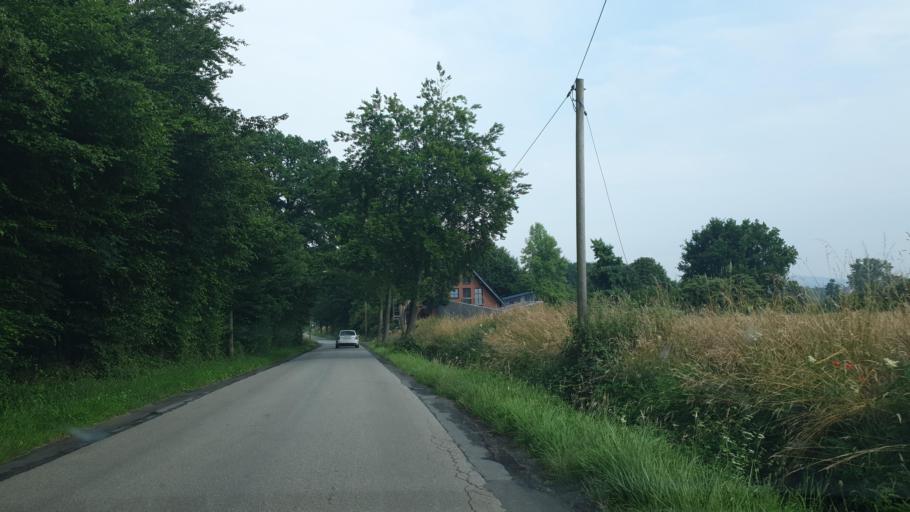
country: DE
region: North Rhine-Westphalia
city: Bad Oeynhausen
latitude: 52.2420
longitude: 8.7579
